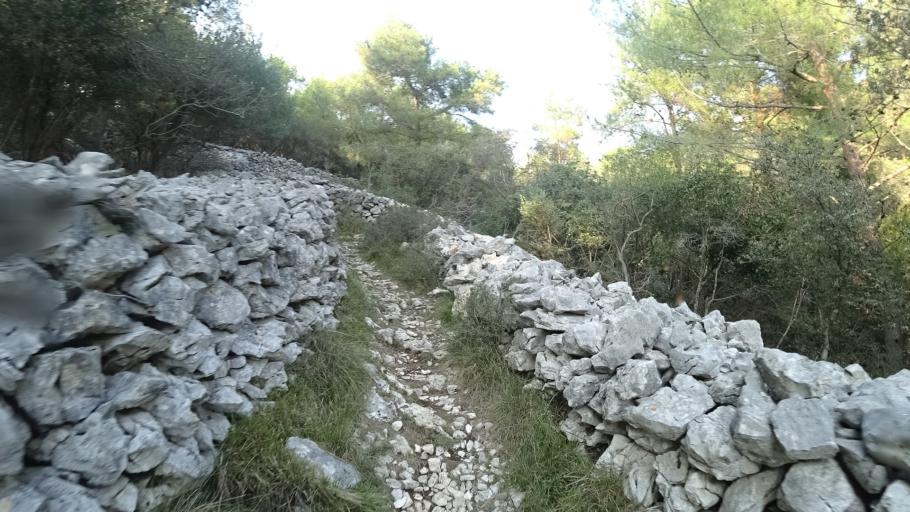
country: HR
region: Primorsko-Goranska
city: Mali Losinj
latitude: 44.5163
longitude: 14.4766
